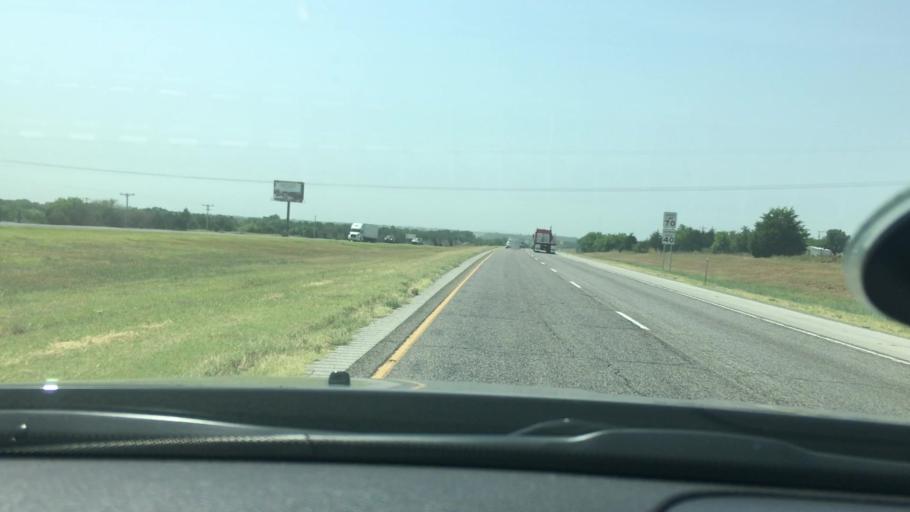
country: US
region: Oklahoma
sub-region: Garvin County
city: Wynnewood
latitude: 34.6131
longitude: -97.2136
